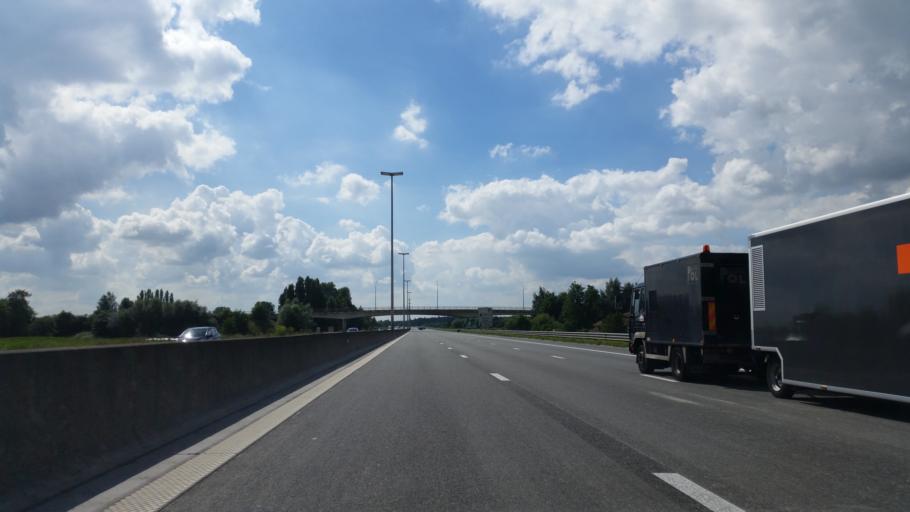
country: BE
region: Flanders
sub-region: Provincie Oost-Vlaanderen
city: De Pinte
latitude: 50.9805
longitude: 3.6521
